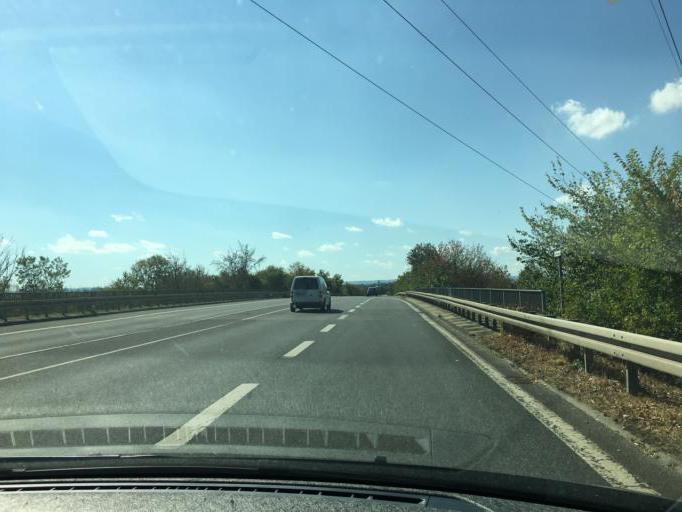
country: DE
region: North Rhine-Westphalia
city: Zulpich
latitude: 50.7124
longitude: 6.6779
